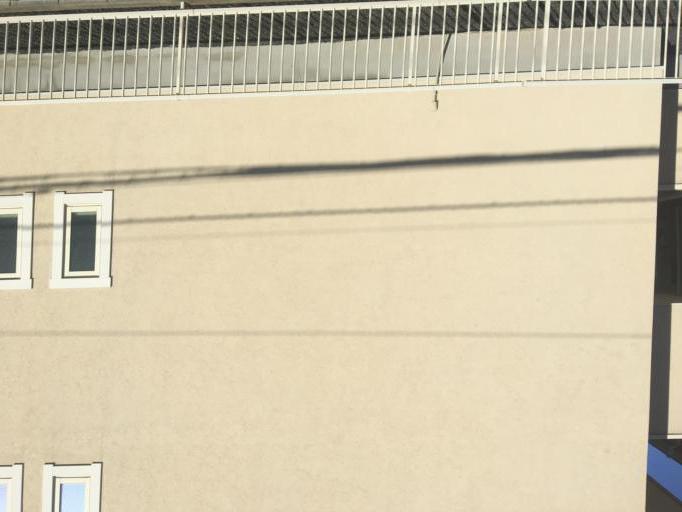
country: JP
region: Chiba
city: Funabashi
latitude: 35.6845
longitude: 140.0117
